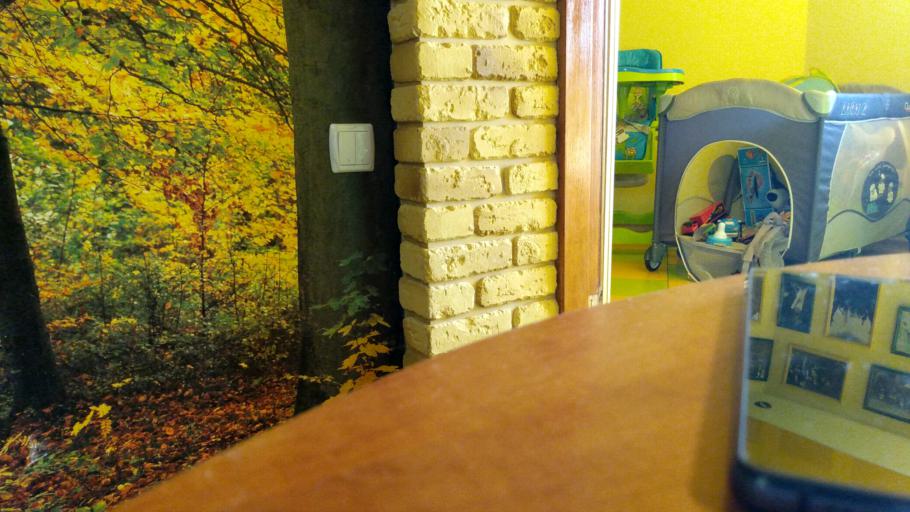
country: RU
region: Tverskaya
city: Kalashnikovo
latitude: 57.2789
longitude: 35.3763
